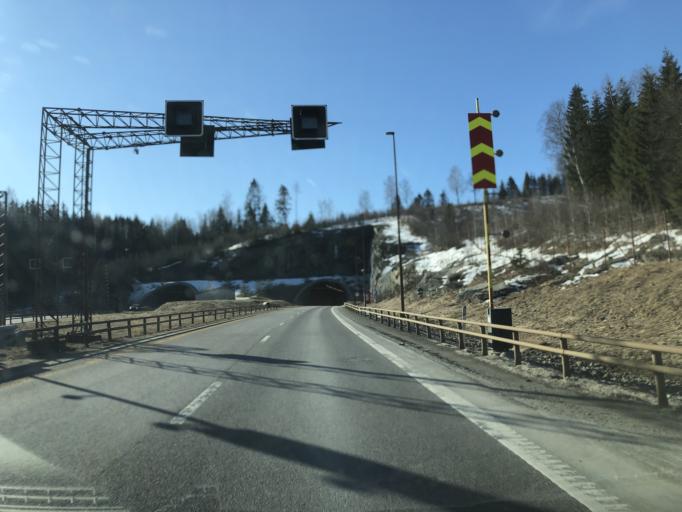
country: NO
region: Akershus
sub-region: Eidsvoll
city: Eidsvoll
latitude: 60.3477
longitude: 11.2082
